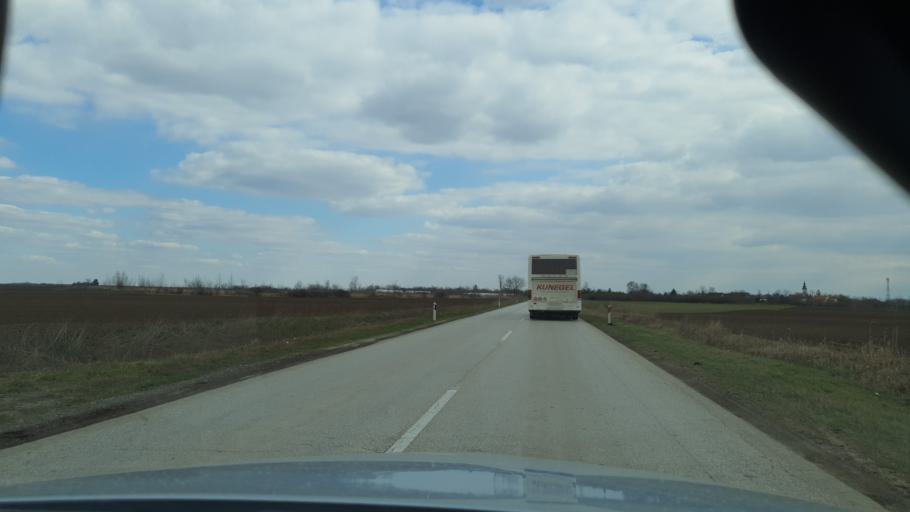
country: RS
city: Obrovac
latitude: 45.4218
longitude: 19.3959
